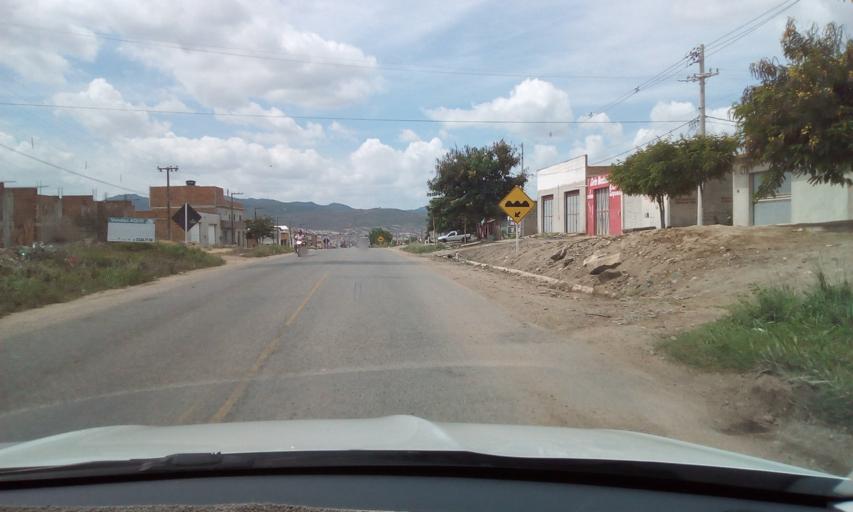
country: BR
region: Pernambuco
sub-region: Bezerros
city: Bezerros
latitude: -8.2552
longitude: -35.7576
